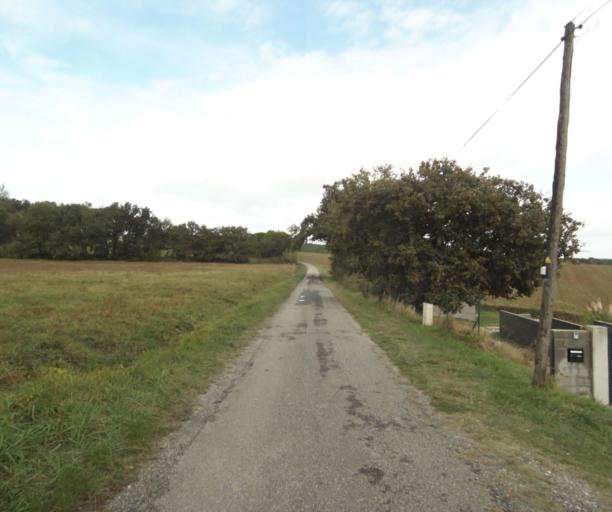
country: FR
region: Midi-Pyrenees
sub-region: Departement du Tarn-et-Garonne
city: Beaumont-de-Lomagne
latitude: 43.8650
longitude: 1.0990
